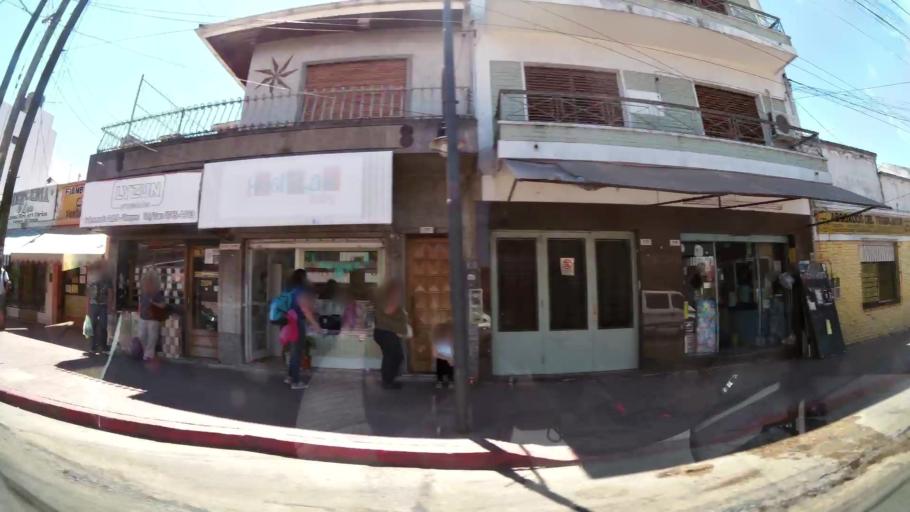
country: AR
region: Buenos Aires
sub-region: Partido de Tigre
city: Tigre
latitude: -34.4522
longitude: -58.5543
